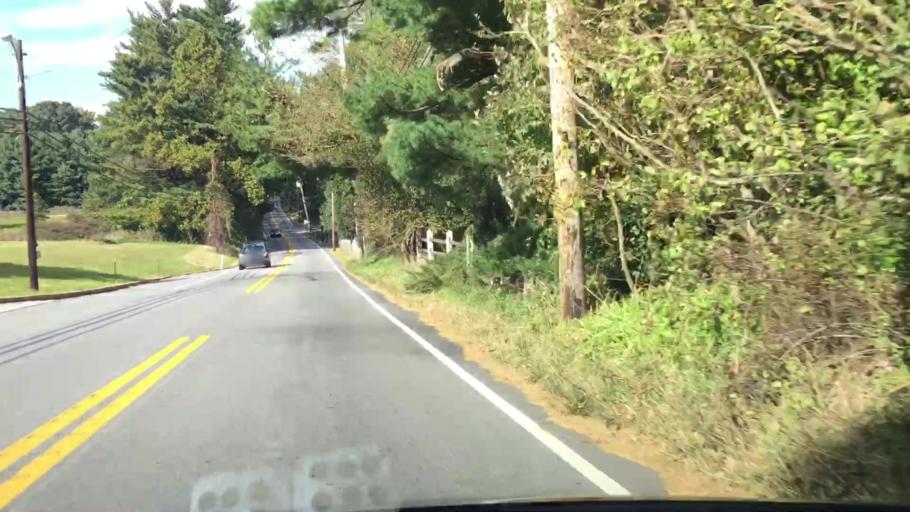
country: US
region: Pennsylvania
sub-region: Delaware County
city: Media
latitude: 39.9434
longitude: -75.3976
